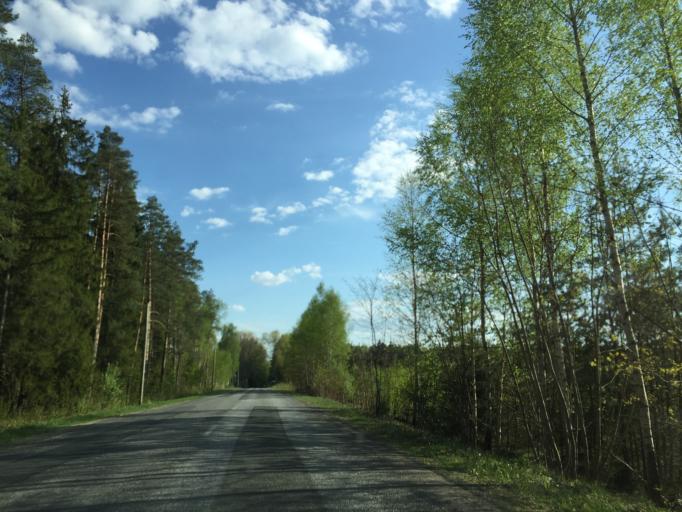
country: LV
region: Sigulda
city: Sigulda
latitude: 57.2005
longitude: 24.8503
